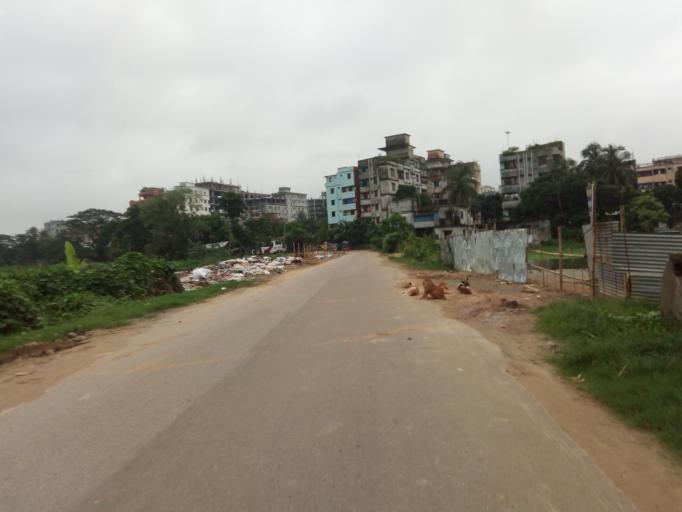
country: BD
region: Dhaka
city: Tungi
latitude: 23.8500
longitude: 90.4160
